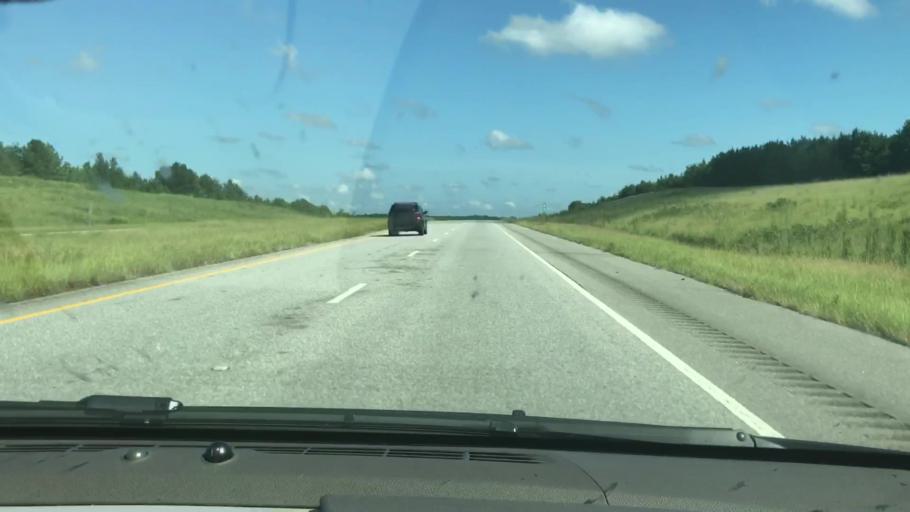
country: US
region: Alabama
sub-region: Barbour County
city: Eufaula
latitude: 32.1750
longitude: -85.1771
